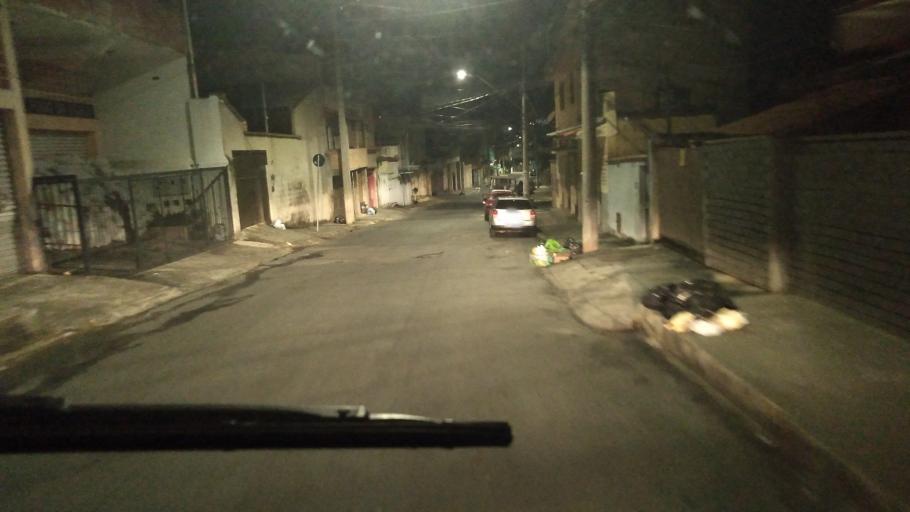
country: BR
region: Minas Gerais
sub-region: Belo Horizonte
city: Belo Horizonte
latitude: -19.8748
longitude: -43.9416
